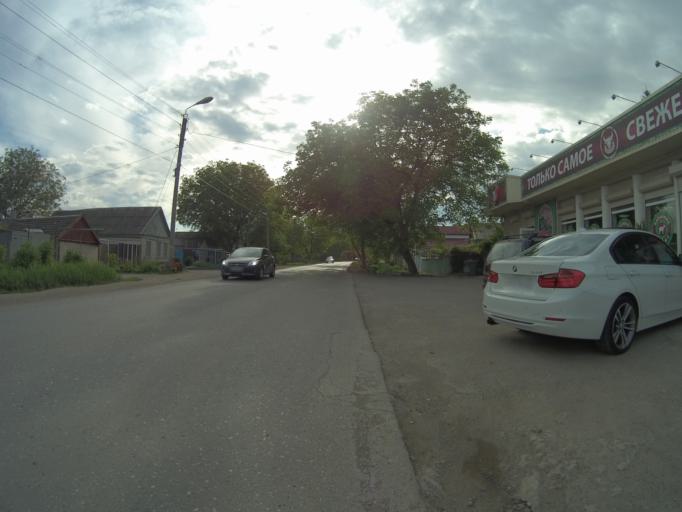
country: RU
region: Stavropol'skiy
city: Svobody
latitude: 44.0400
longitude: 43.0142
